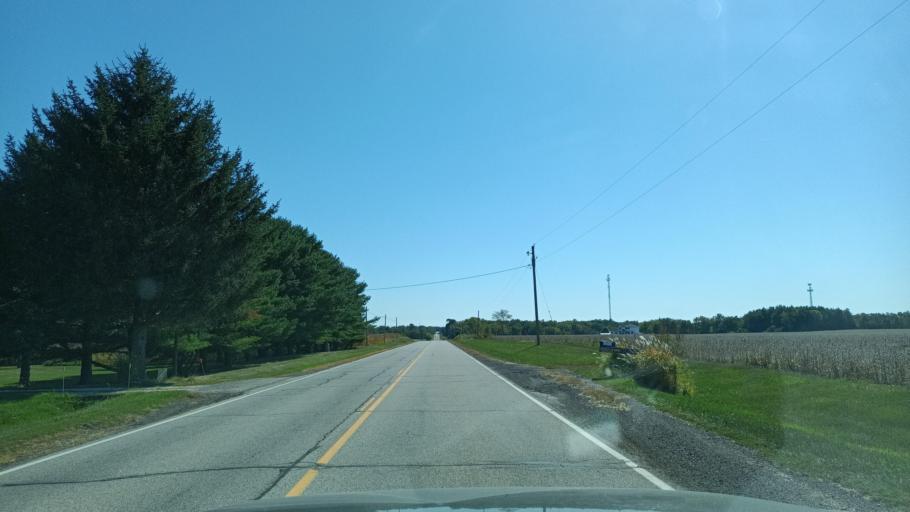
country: US
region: Illinois
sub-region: Peoria County
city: Elmwood
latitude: 40.8506
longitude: -89.9170
